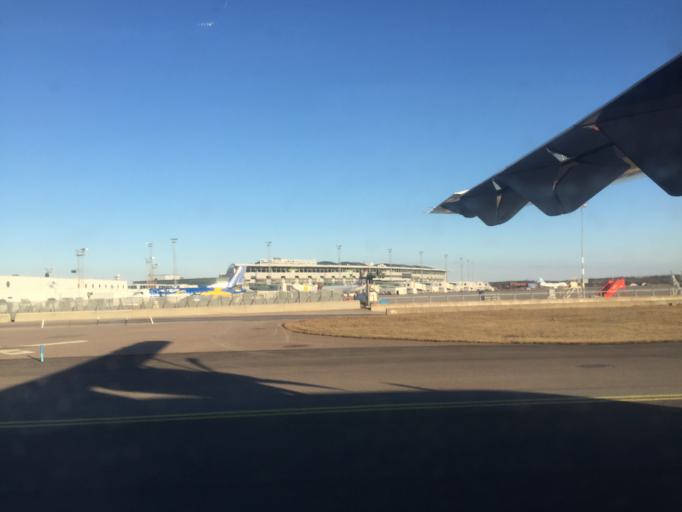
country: SE
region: Stockholm
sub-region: Sigtuna Kommun
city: Marsta
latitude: 59.6452
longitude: 17.9215
